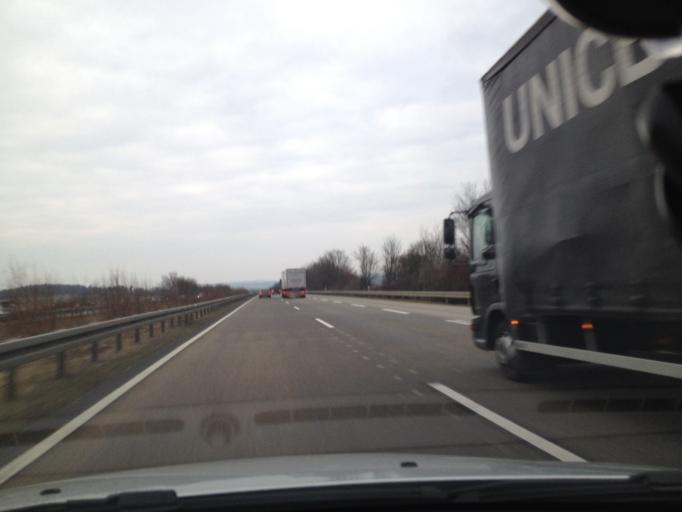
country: DE
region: Hesse
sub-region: Regierungsbezirk Darmstadt
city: Munzenberg
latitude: 50.4418
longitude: 8.7964
